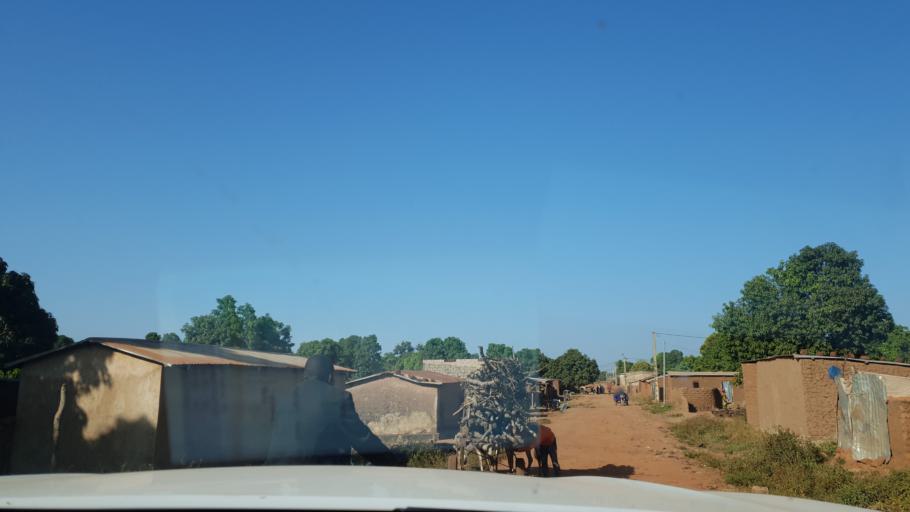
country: ML
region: Sikasso
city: Kadiolo
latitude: 10.8907
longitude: -5.6032
